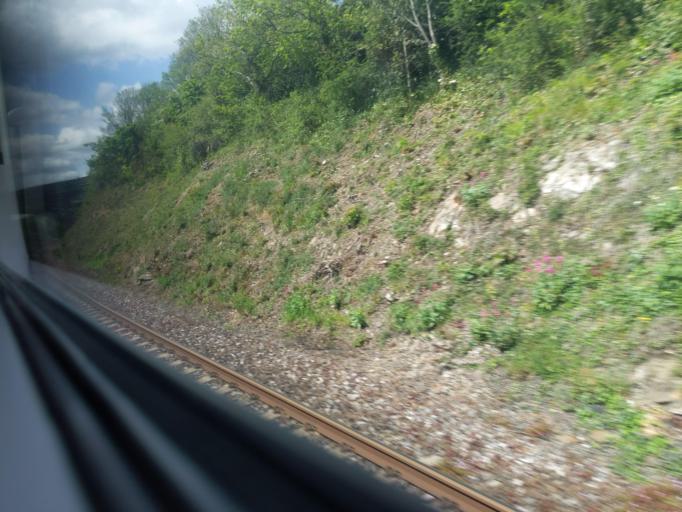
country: GB
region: England
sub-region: Cornwall
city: Saltash
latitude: 50.3974
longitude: -4.2248
